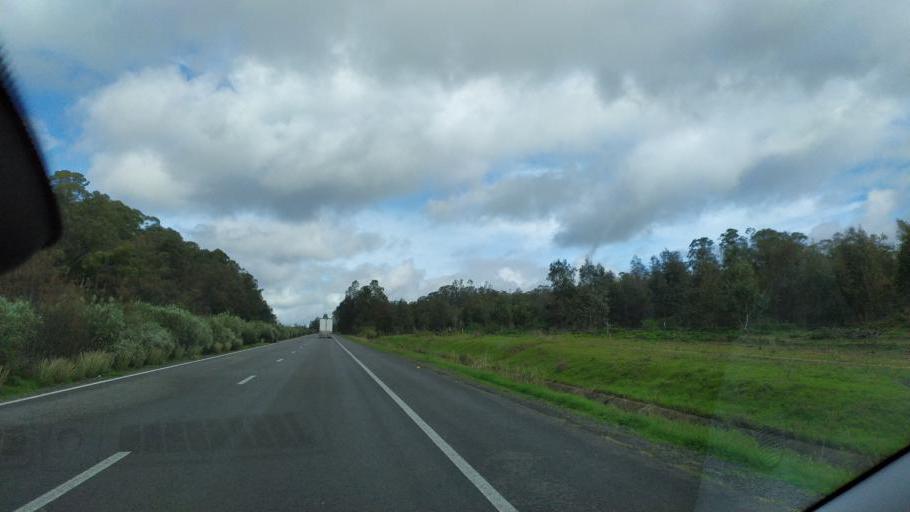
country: MA
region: Gharb-Chrarda-Beni Hssen
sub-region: Kenitra Province
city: Lalla Mimouna
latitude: 34.9266
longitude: -6.2027
